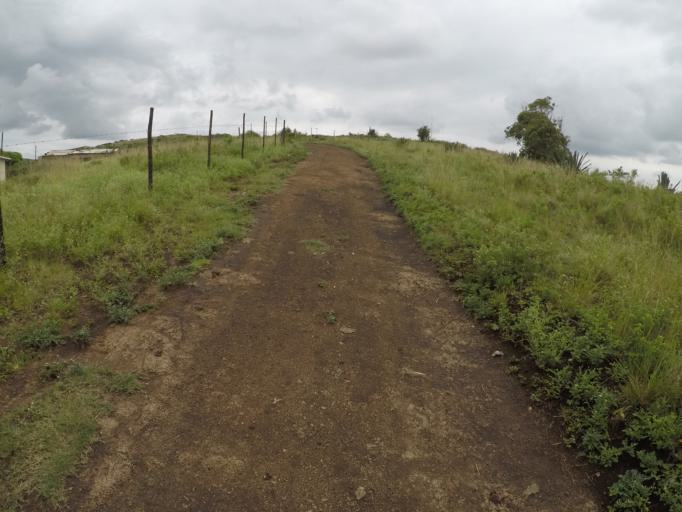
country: ZA
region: KwaZulu-Natal
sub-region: uThungulu District Municipality
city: Empangeni
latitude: -28.7074
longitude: 31.8516
